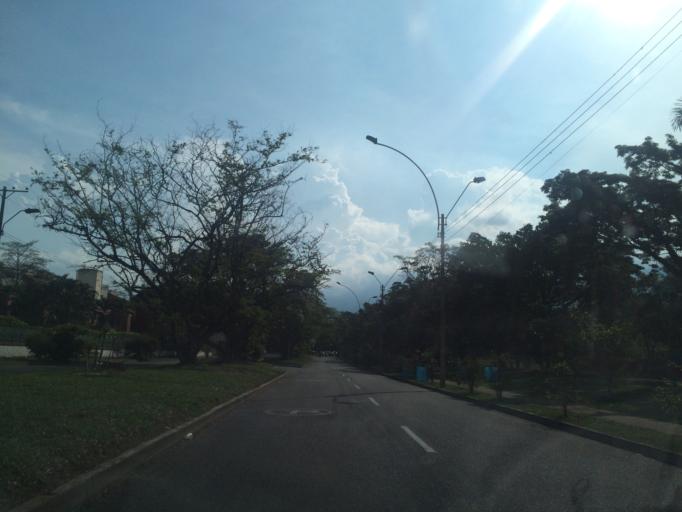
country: CO
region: Valle del Cauca
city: Cali
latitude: 3.3836
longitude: -76.5360
